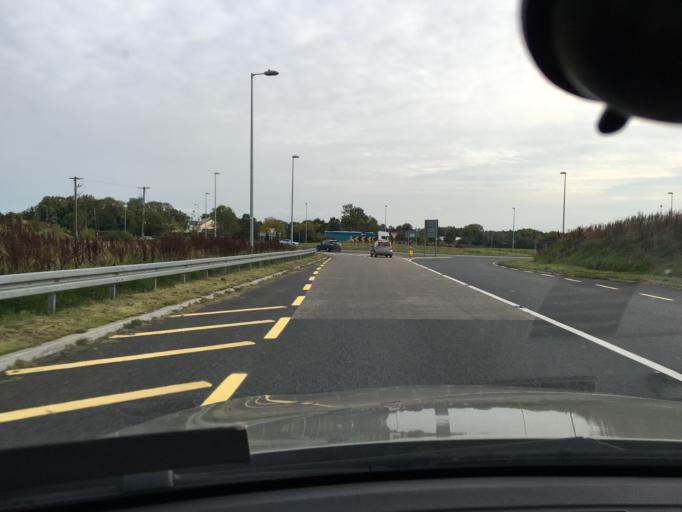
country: IE
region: Leinster
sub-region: An Longfort
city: Longford
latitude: 53.7258
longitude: -7.8256
